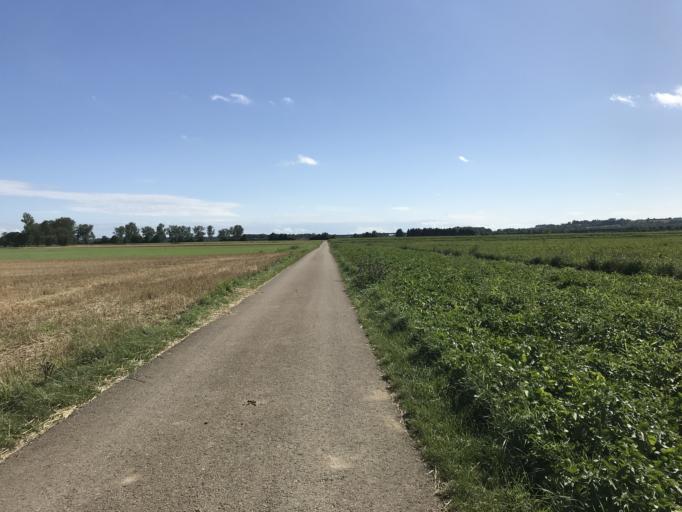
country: DE
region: Baden-Wuerttemberg
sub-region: Tuebingen Region
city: Langenau
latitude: 48.4788
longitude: 10.1225
